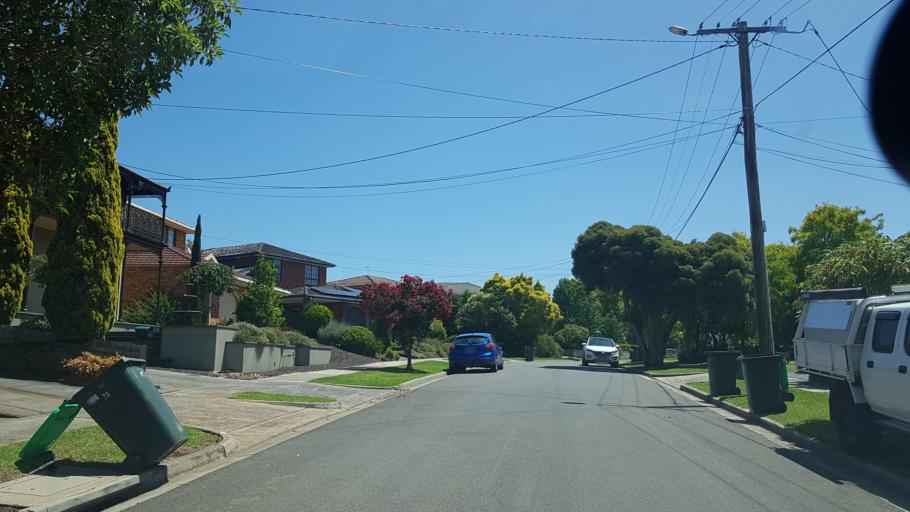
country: AU
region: Victoria
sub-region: Manningham
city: Bulleen
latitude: -37.7568
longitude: 145.0971
